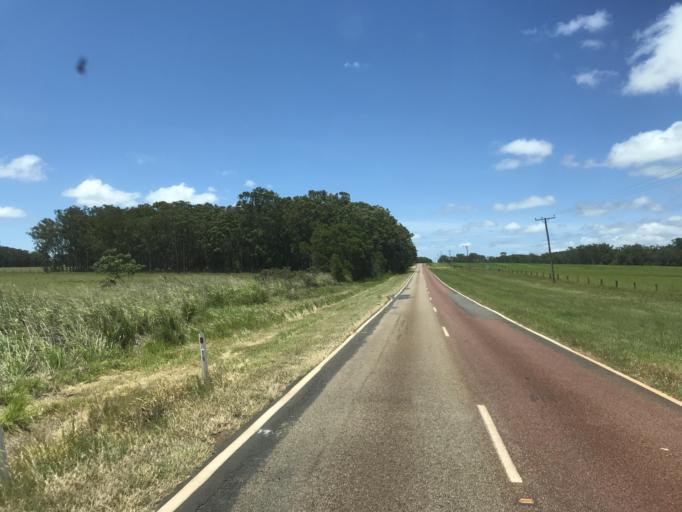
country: AU
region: Queensland
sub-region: Tablelands
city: Ravenshoe
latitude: -17.5260
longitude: 145.4538
